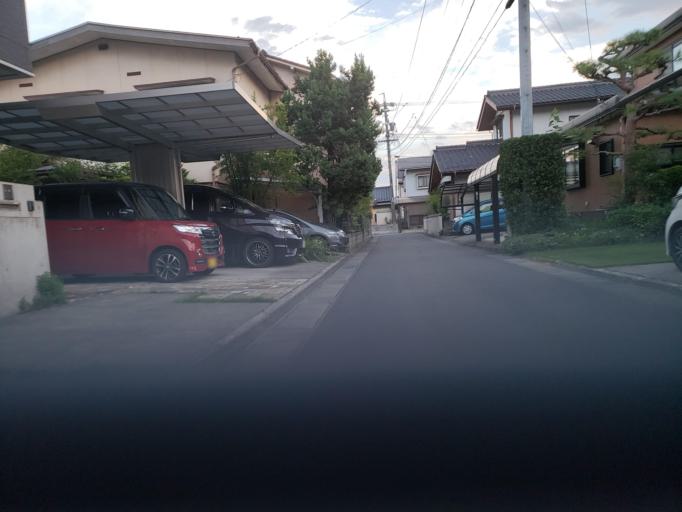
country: JP
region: Nagano
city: Nagano-shi
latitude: 36.6267
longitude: 138.1608
